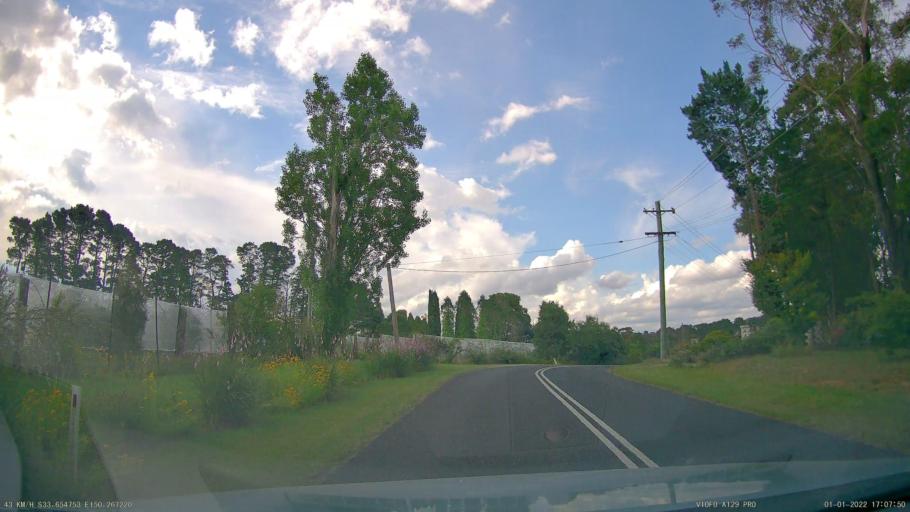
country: AU
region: New South Wales
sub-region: Blue Mountains Municipality
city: Blackheath
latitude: -33.6546
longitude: 150.2672
